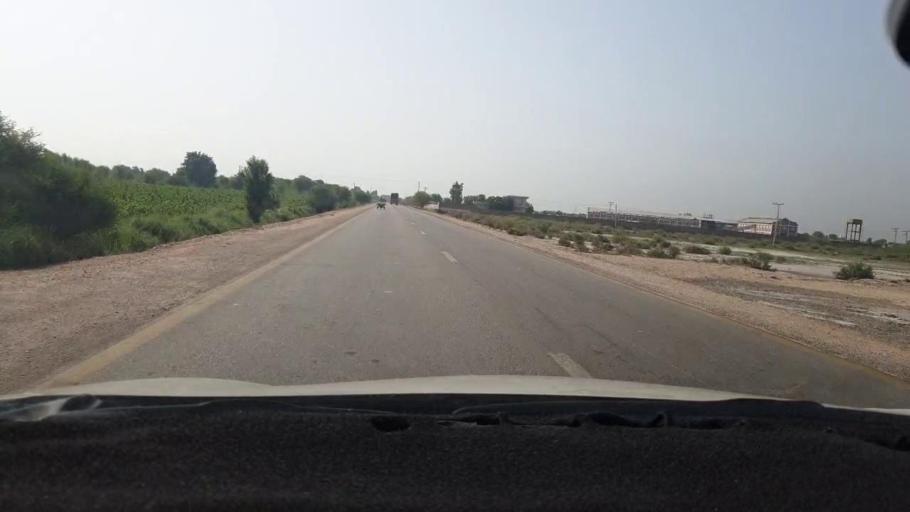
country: PK
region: Sindh
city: Sanghar
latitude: 26.0086
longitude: 68.9598
